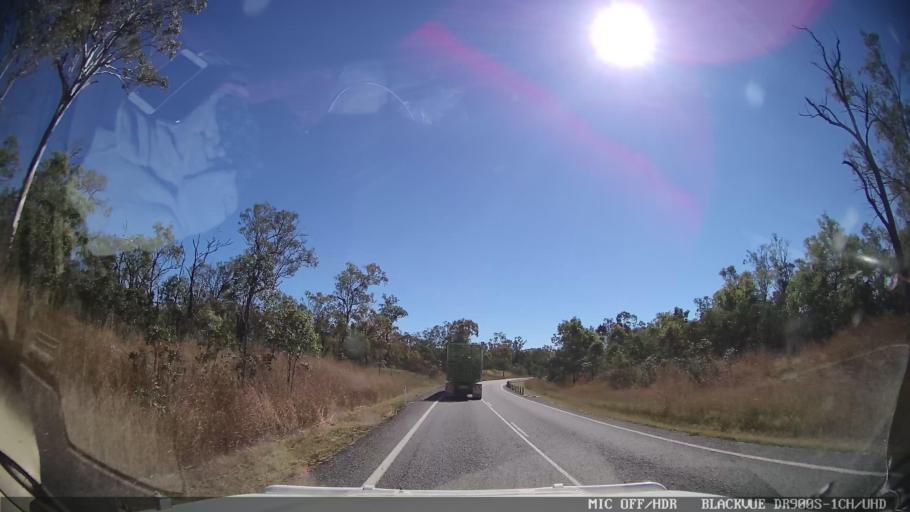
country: AU
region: Queensland
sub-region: Gladstone
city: Toolooa
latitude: -24.1561
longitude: 151.2124
